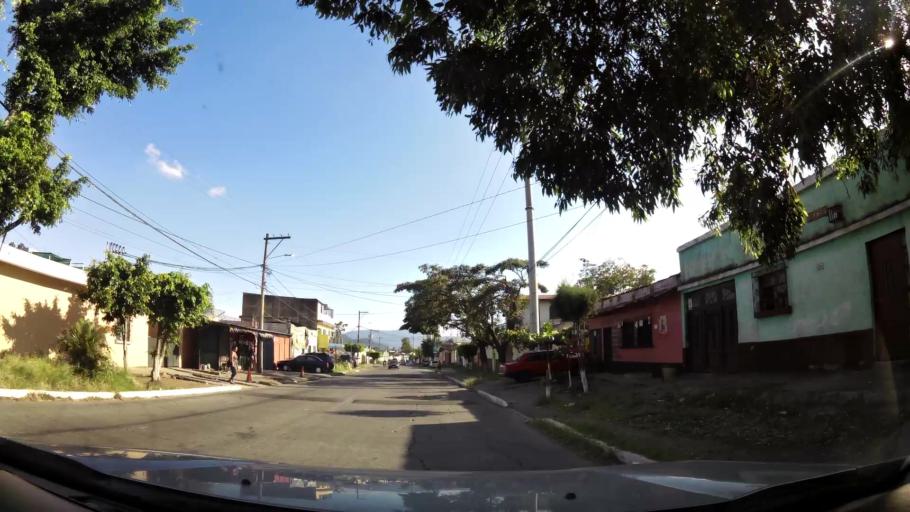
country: GT
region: Guatemala
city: Villa Nueva
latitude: 14.5202
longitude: -90.5745
